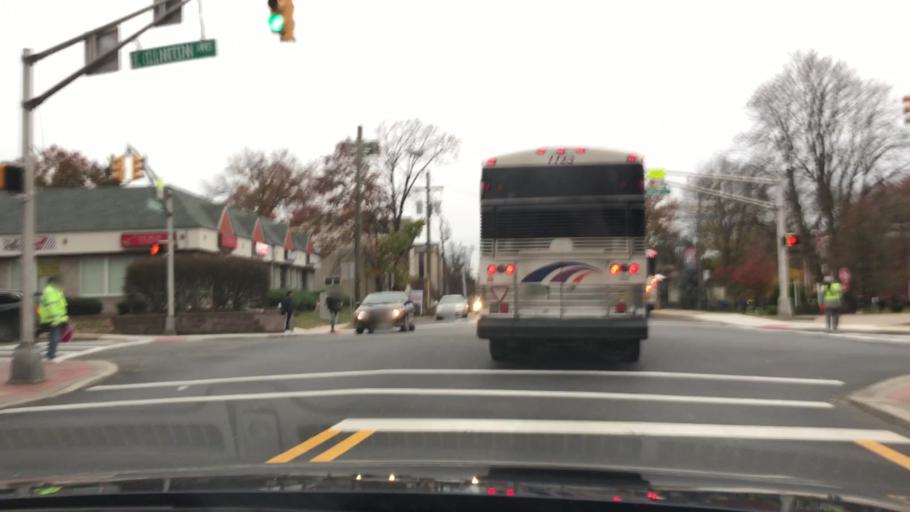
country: US
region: New Jersey
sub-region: Bergen County
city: Bergenfield
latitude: 40.9240
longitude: -73.9970
